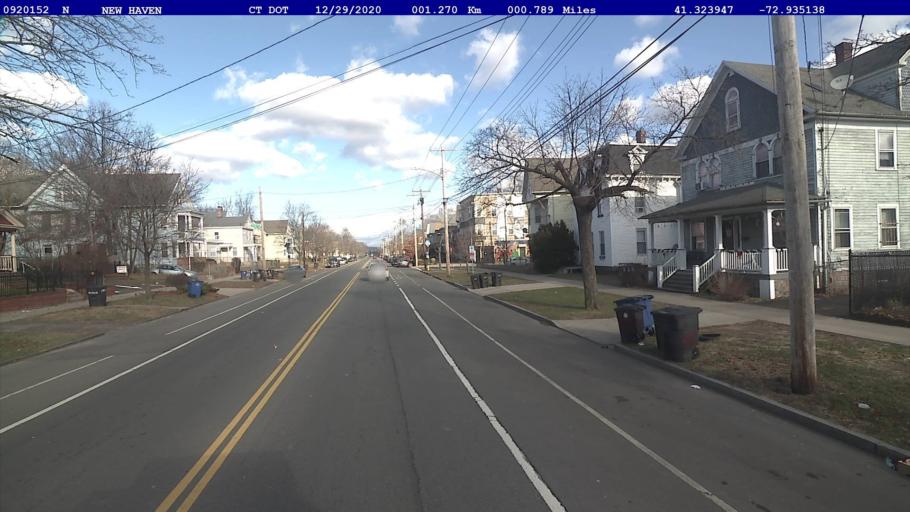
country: US
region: Connecticut
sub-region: New Haven County
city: New Haven
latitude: 41.3240
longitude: -72.9351
